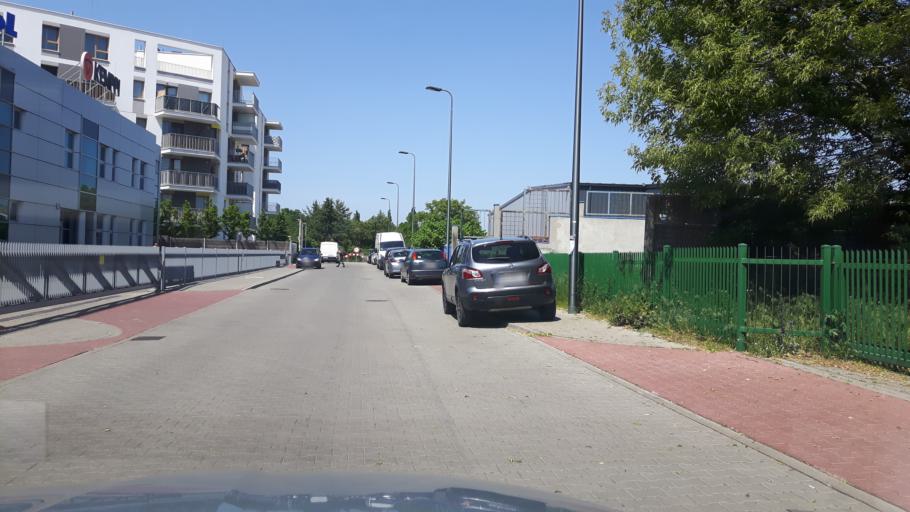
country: PL
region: Masovian Voivodeship
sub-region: Warszawa
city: Targowek
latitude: 52.2770
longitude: 21.0465
